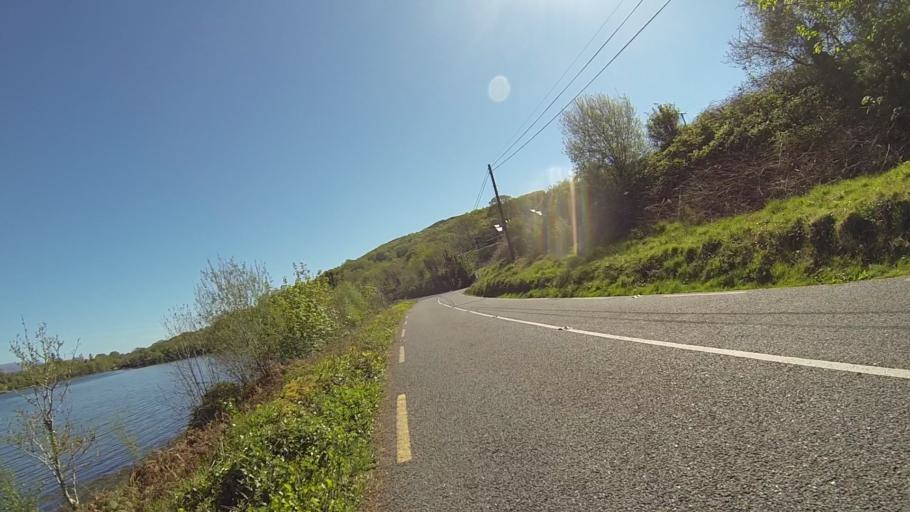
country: IE
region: Munster
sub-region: Ciarrai
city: Kenmare
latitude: 51.8444
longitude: -9.6475
